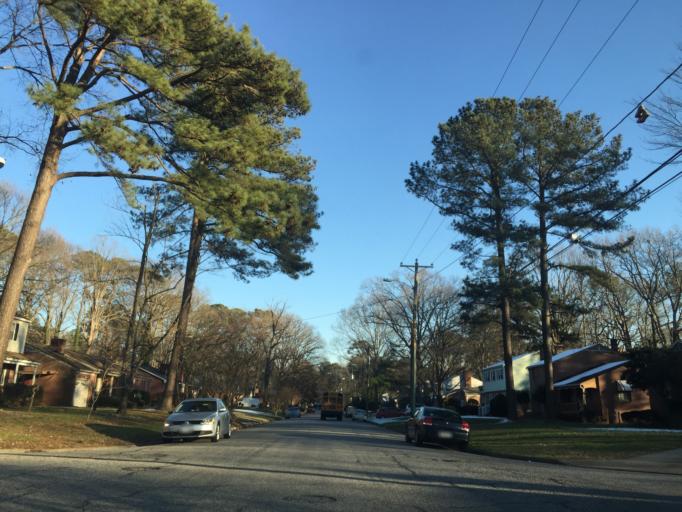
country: US
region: Virginia
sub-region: City of Newport News
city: Newport News
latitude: 37.0842
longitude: -76.4952
